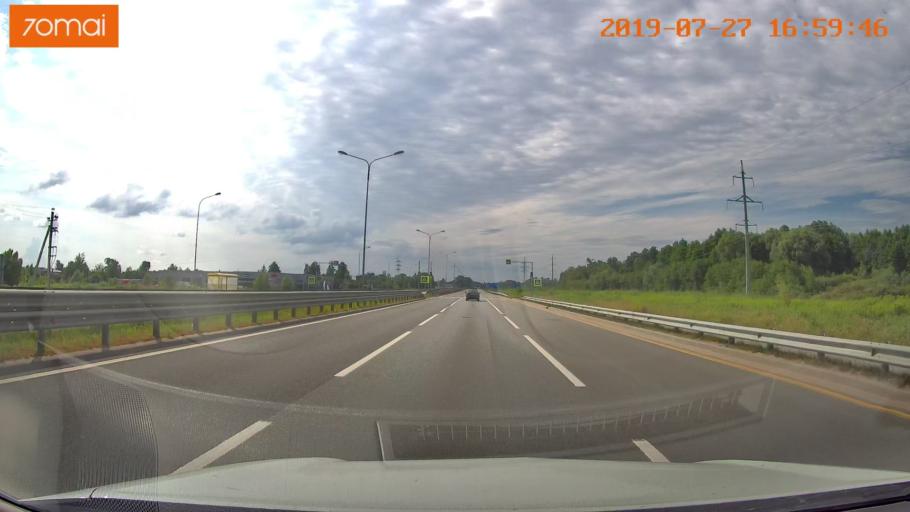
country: RU
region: Kaliningrad
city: Bol'shoe Isakovo
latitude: 54.7057
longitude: 20.6416
